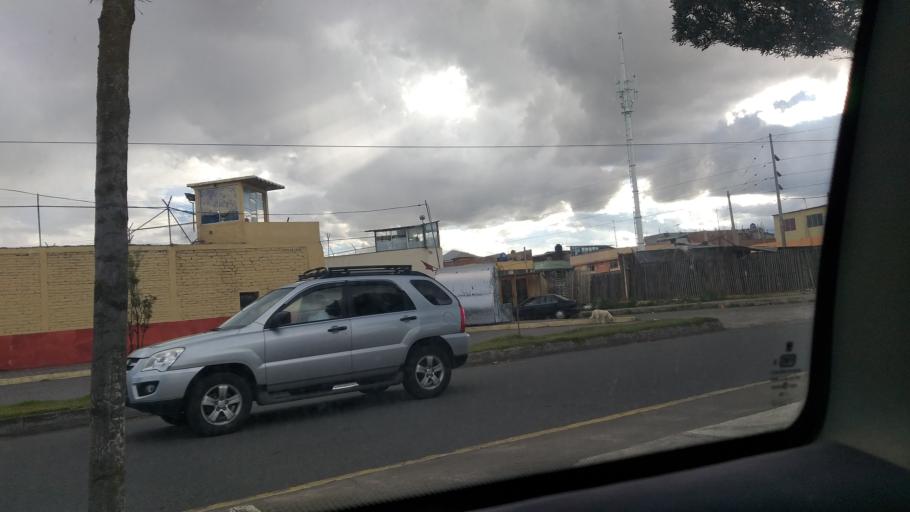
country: EC
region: Chimborazo
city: Riobamba
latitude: -1.6902
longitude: -78.6313
